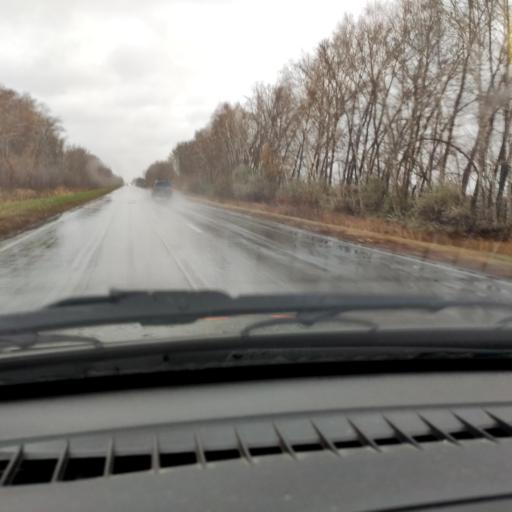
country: RU
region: Samara
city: Tol'yatti
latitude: 53.6098
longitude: 49.3167
